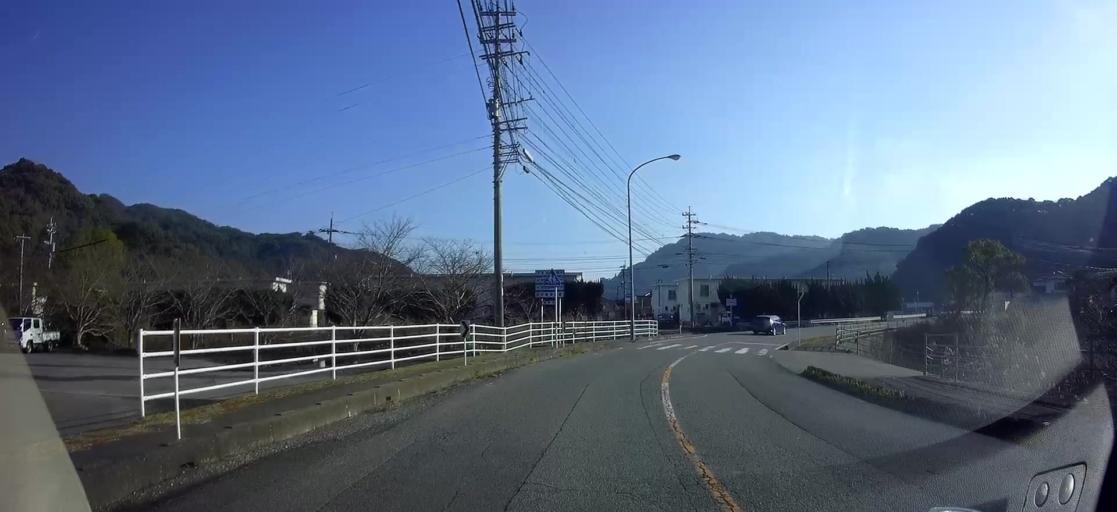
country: JP
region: Kumamoto
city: Hondo
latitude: 32.4284
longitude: 130.4024
